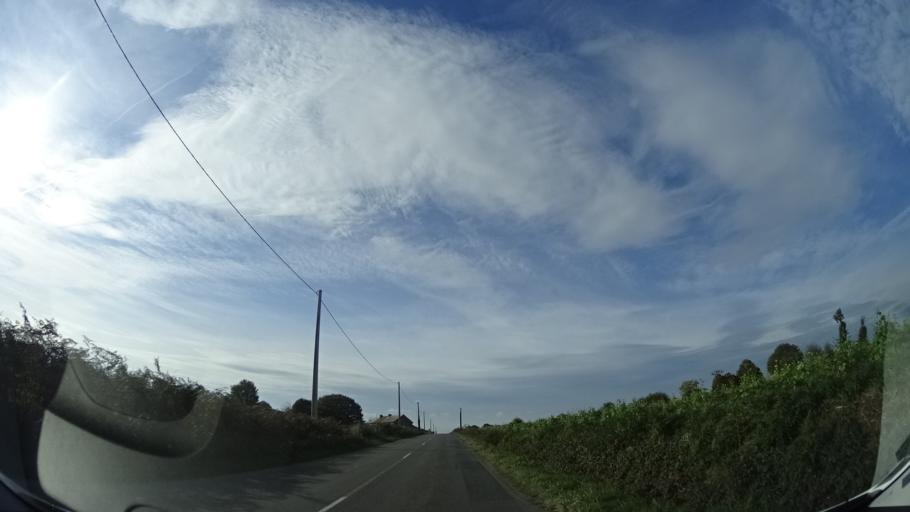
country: FR
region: Brittany
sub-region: Departement d'Ille-et-Vilaine
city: Romille
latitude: 48.2165
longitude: -1.8605
